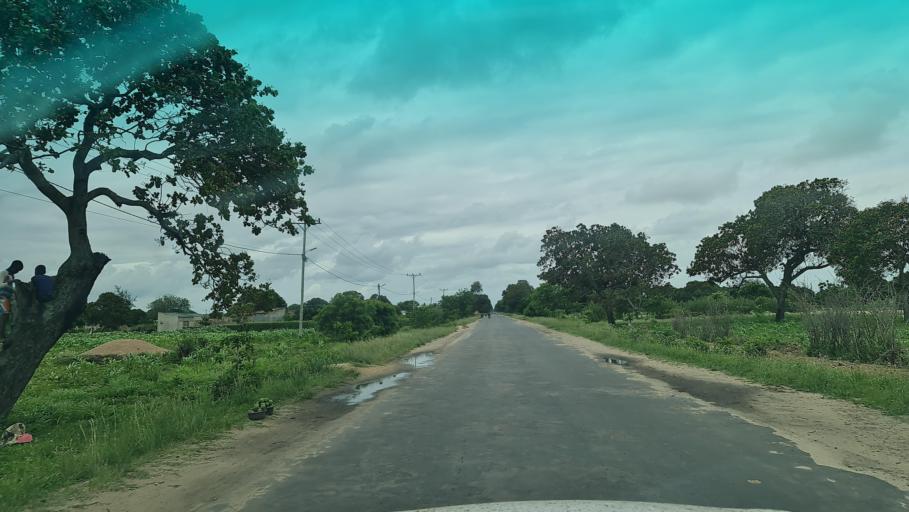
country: MZ
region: Maputo
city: Manhica
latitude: -25.4240
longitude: 32.7727
